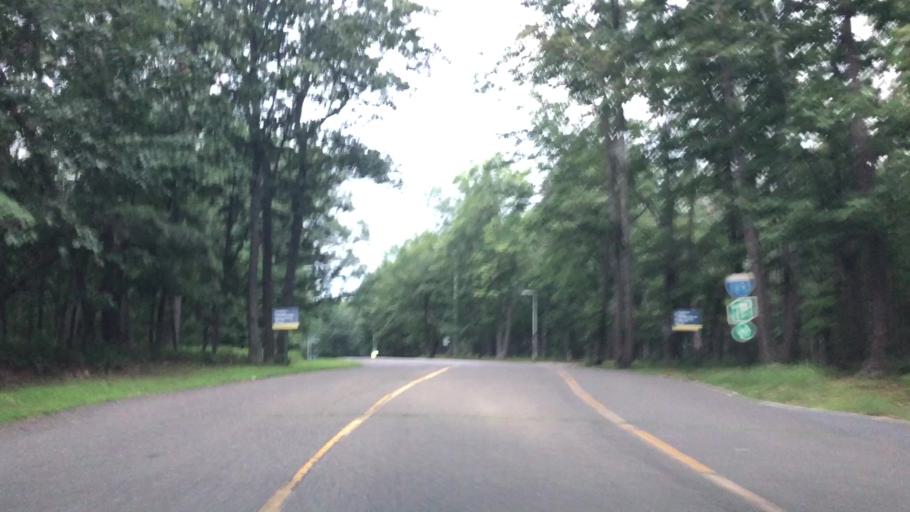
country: US
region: New Jersey
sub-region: Monmouth County
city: Shrewsbury
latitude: 40.1444
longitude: -74.4424
